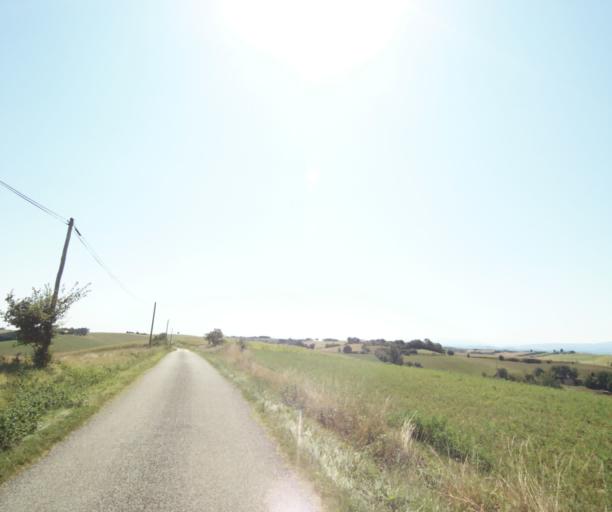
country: FR
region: Midi-Pyrenees
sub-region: Departement de l'Ariege
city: Lezat-sur-Leze
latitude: 43.2565
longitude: 1.3988
